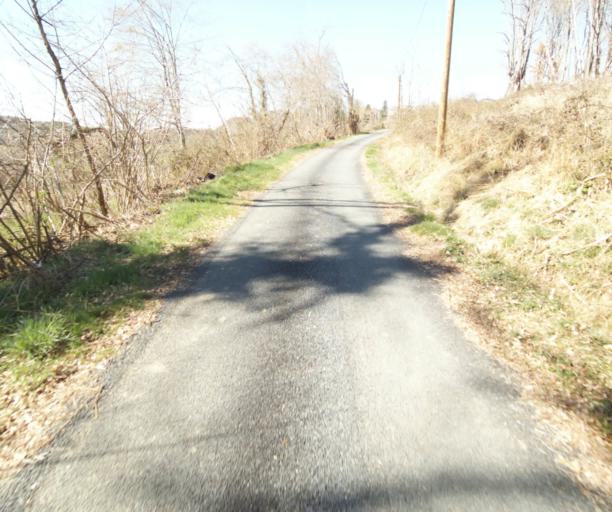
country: FR
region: Limousin
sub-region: Departement de la Correze
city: Chamboulive
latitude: 45.4401
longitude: 1.7265
